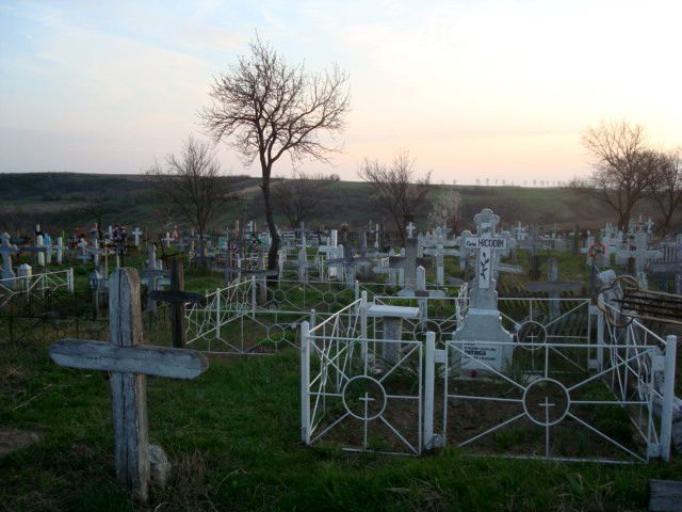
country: RO
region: Galati
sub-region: Comuna Radesti
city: Radesti
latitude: 46.0687
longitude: 27.7835
